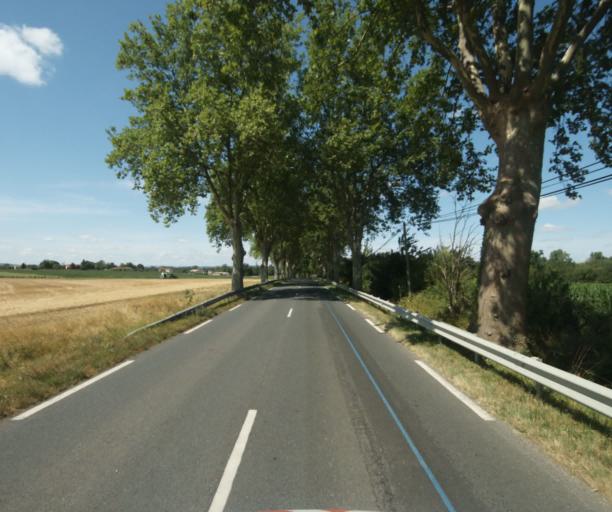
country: FR
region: Midi-Pyrenees
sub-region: Departement de la Haute-Garonne
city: Revel
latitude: 43.4797
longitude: 2.0148
